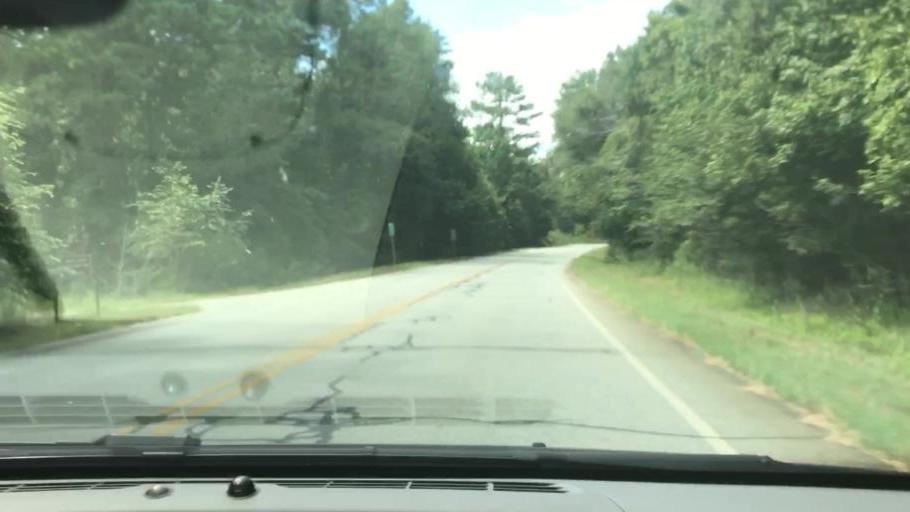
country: US
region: Georgia
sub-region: Stewart County
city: Lumpkin
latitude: 32.1390
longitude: -84.8471
